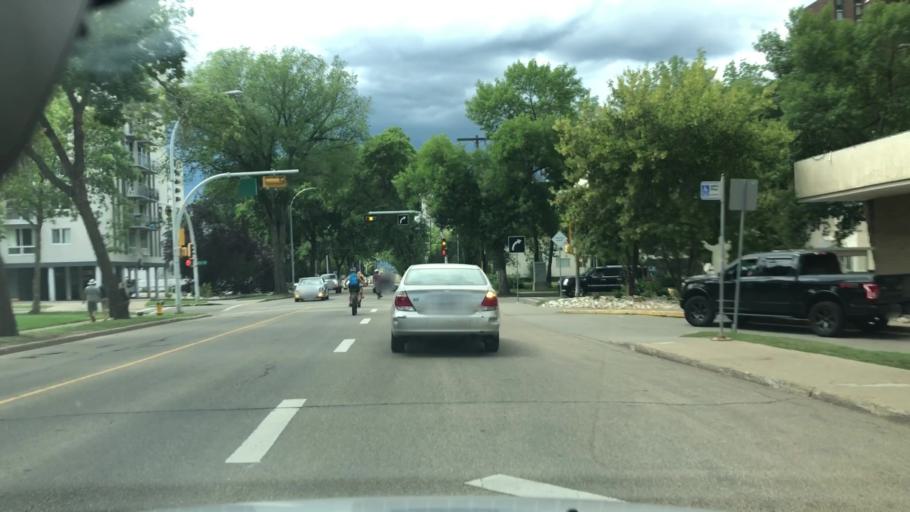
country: CA
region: Alberta
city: Edmonton
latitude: 53.5388
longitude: -113.5132
